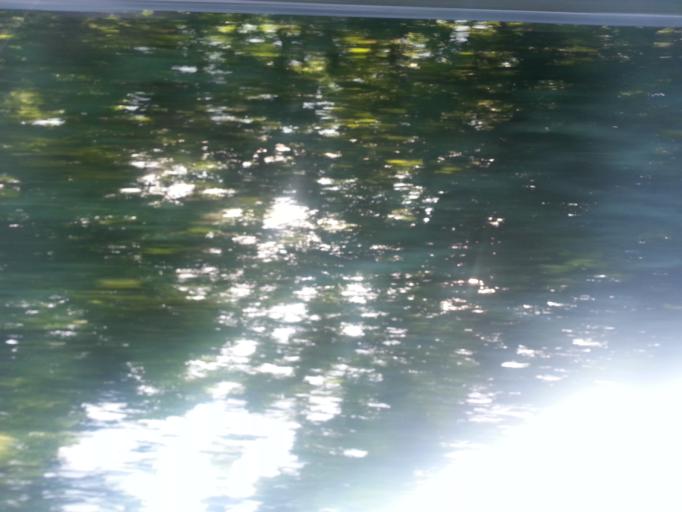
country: US
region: Tennessee
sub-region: Blount County
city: Maryville
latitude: 35.6449
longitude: -83.9322
